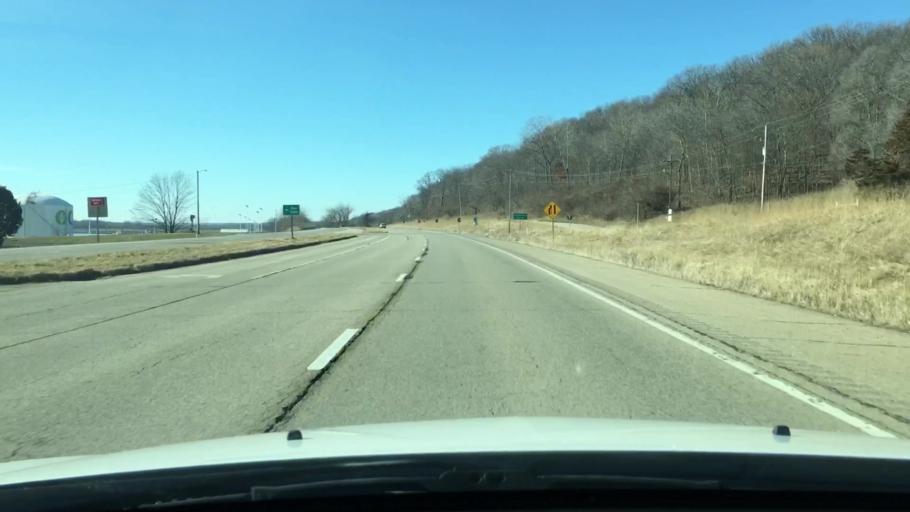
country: US
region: Illinois
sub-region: Peoria County
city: Glasford
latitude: 40.5587
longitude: -89.7752
